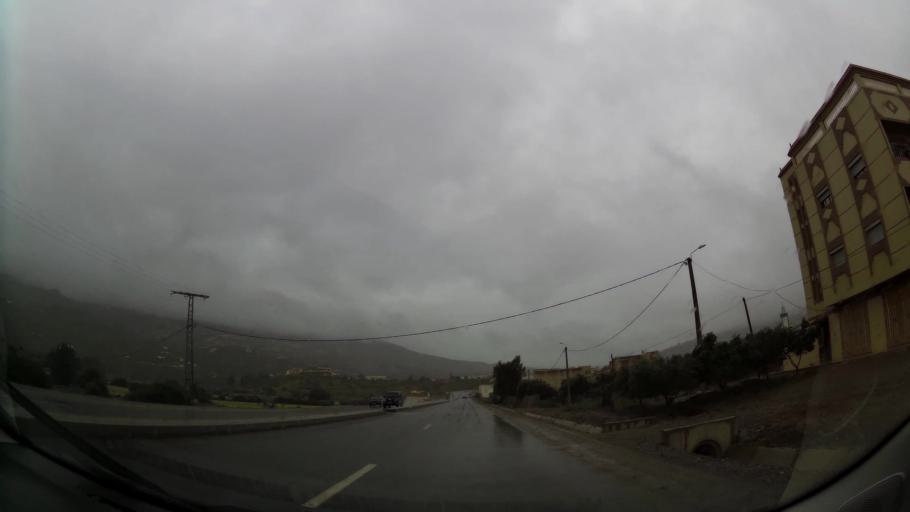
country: MA
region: Taza-Al Hoceima-Taounate
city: Imzourene
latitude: 35.0442
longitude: -3.8238
